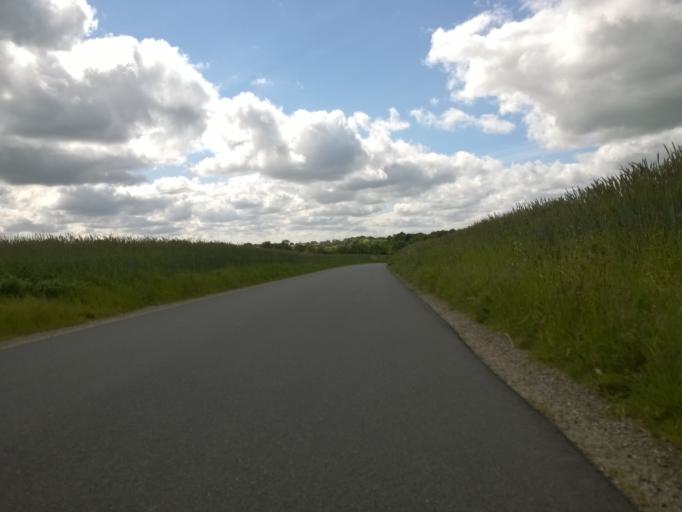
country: DK
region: Central Jutland
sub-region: Holstebro Kommune
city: Vinderup
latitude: 56.4039
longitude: 8.7728
